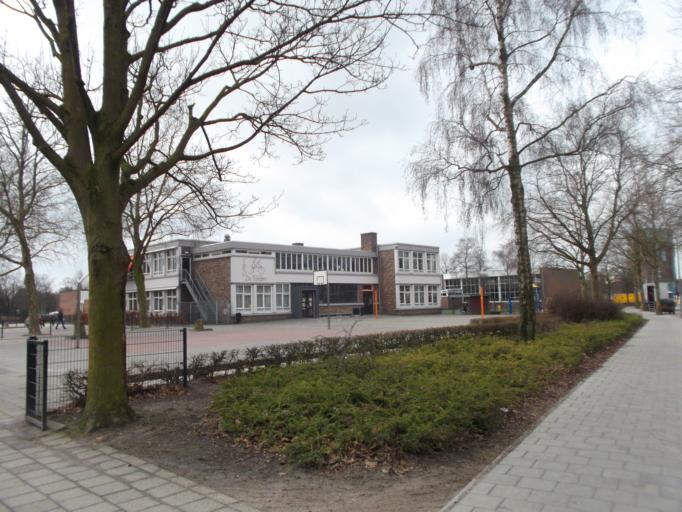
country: NL
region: North Brabant
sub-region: Gemeente Uden
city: Uden
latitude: 51.6613
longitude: 5.6189
